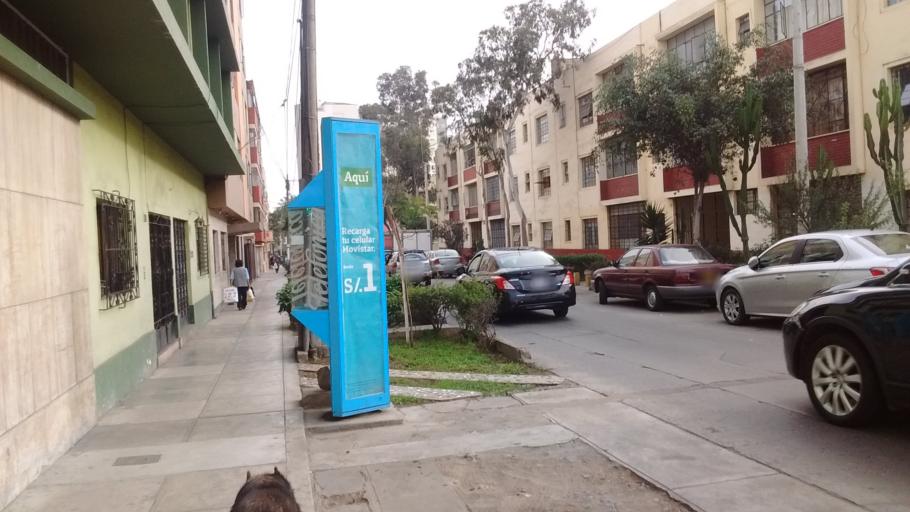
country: PE
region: Lima
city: Lima
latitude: -12.0710
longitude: -77.0447
